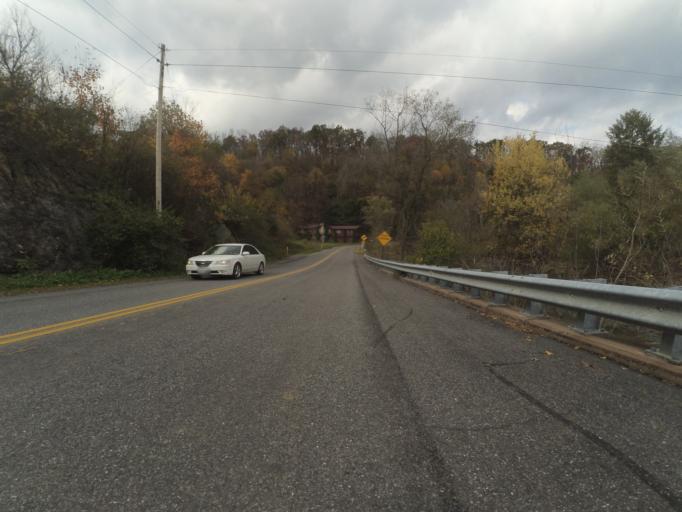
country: US
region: Pennsylvania
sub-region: Centre County
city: Bellefonte
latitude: 40.8900
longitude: -77.7947
